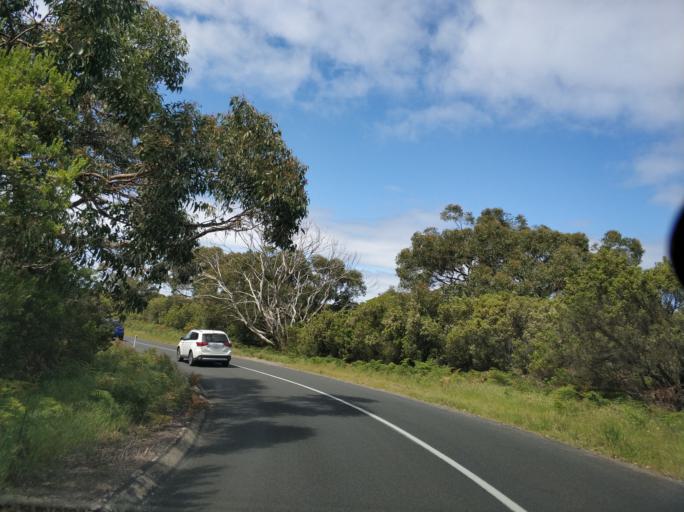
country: AU
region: Victoria
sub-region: Colac-Otway
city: Apollo Bay
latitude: -38.8456
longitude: 143.5327
